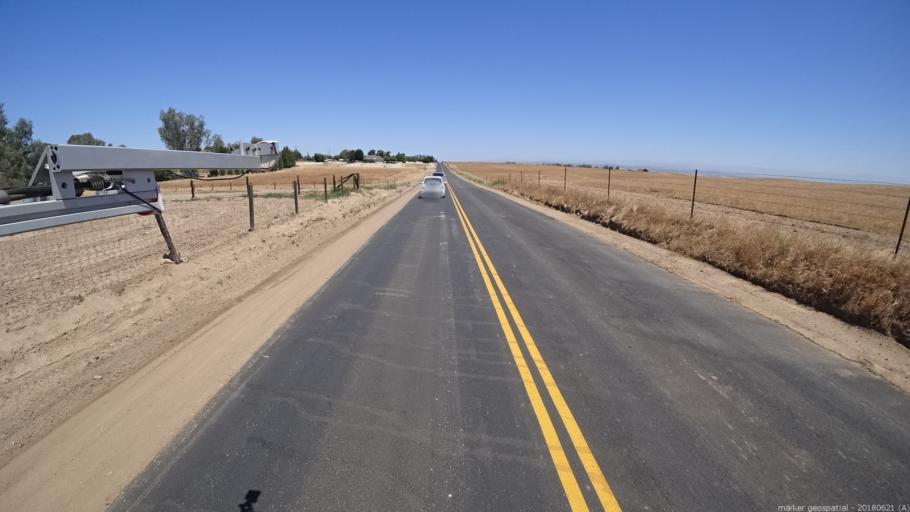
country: US
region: California
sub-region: Madera County
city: Bonadelle Ranchos-Madera Ranchos
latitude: 36.9676
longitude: -119.8758
